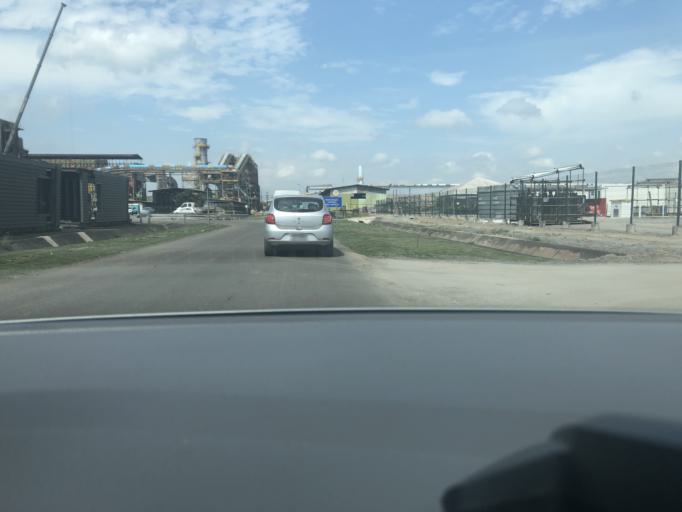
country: BR
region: Rio de Janeiro
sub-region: Itaguai
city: Itaguai
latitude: -22.9127
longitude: -43.7414
